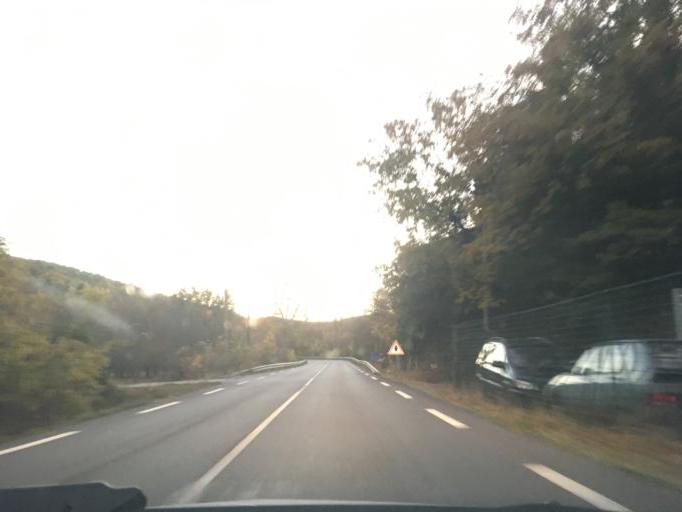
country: FR
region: Provence-Alpes-Cote d'Azur
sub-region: Departement du Var
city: Montferrat
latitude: 43.6055
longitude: 6.4799
